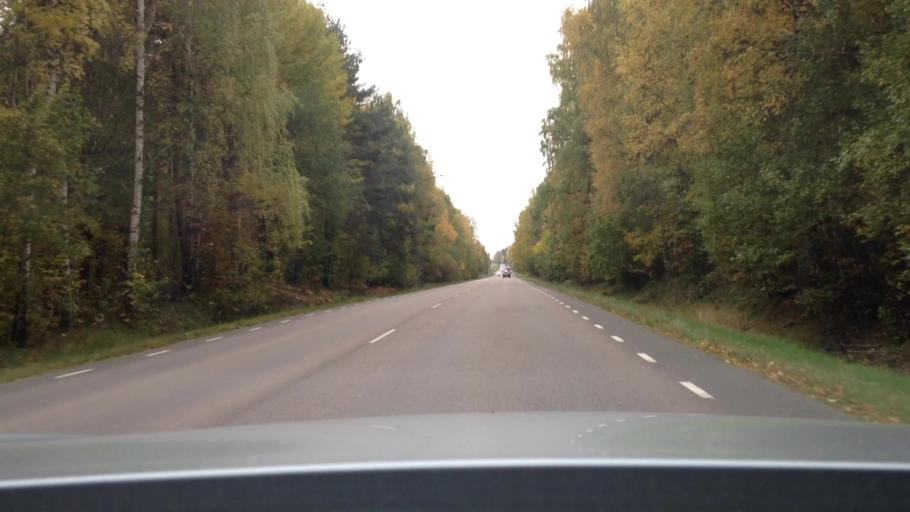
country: SE
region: Vaermland
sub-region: Karlstads Kommun
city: Karlstad
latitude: 59.3751
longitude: 13.4637
